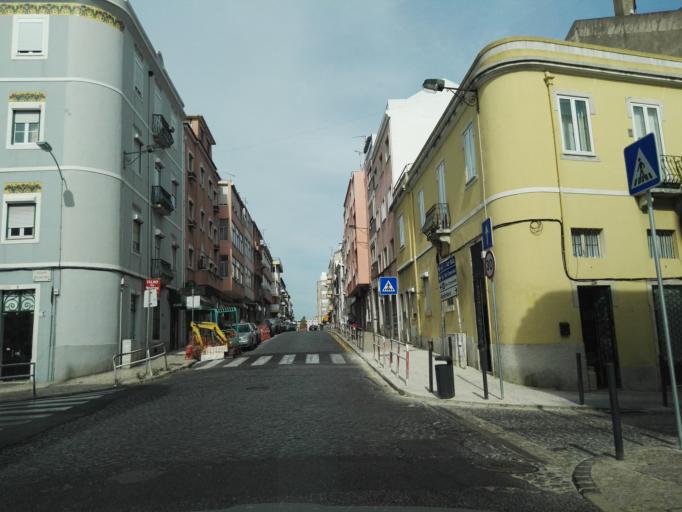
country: PT
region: Lisbon
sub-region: Lisbon
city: Lisbon
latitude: 38.7262
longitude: -9.1648
